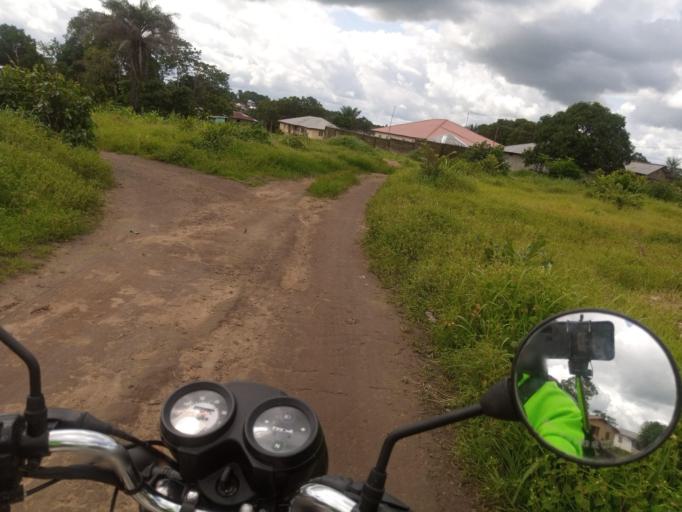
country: SL
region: Northern Province
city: Port Loko
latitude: 8.7762
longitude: -12.7742
